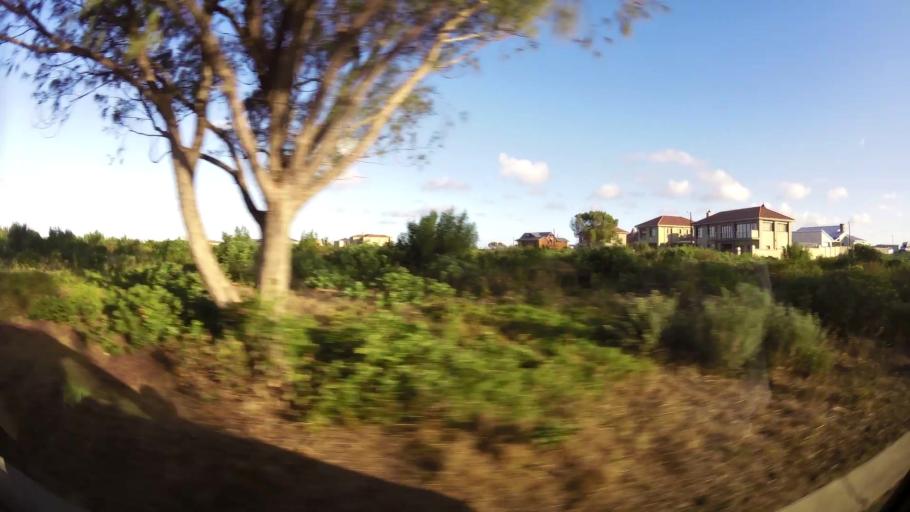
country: ZA
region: Western Cape
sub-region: Eden District Municipality
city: George
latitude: -34.0025
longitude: 22.6521
